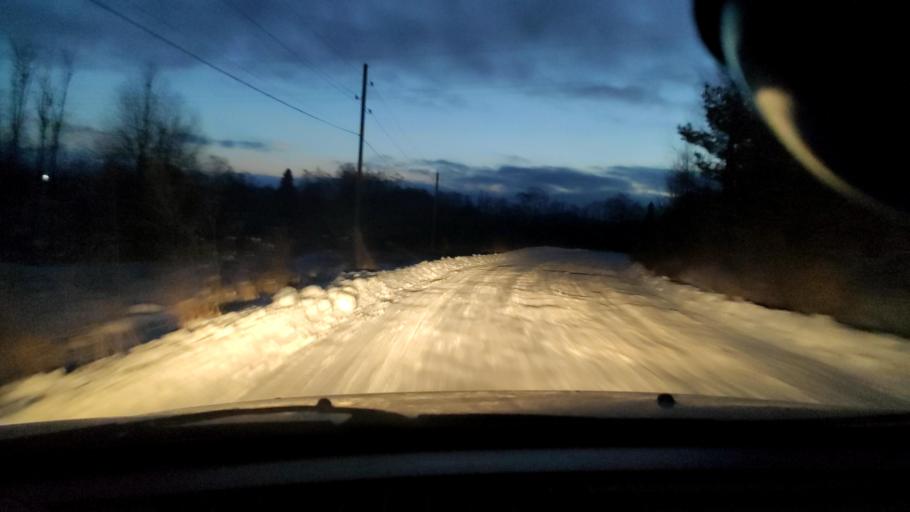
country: RU
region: Perm
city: Kultayevo
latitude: 57.9237
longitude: 55.8729
